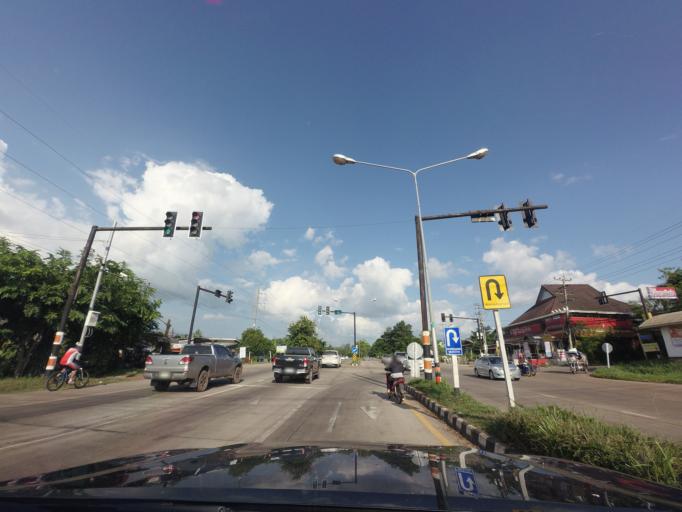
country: TH
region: Nong Khai
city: Nong Khai
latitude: 17.8875
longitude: 102.7687
